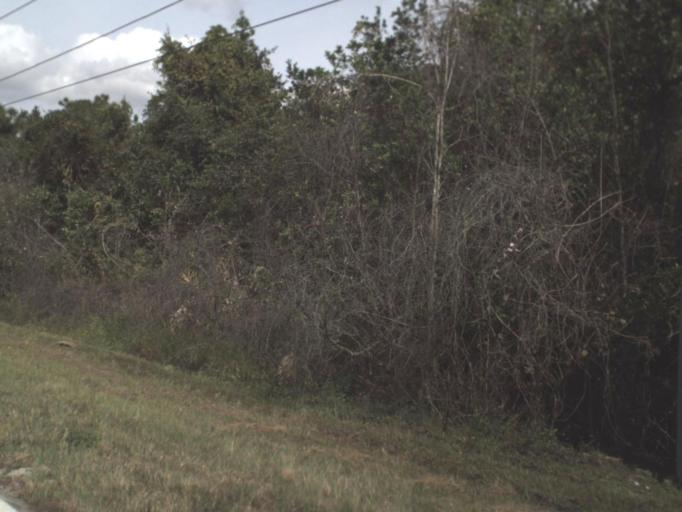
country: US
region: Florida
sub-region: Osceola County
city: Poinciana
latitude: 28.1688
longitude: -81.4472
